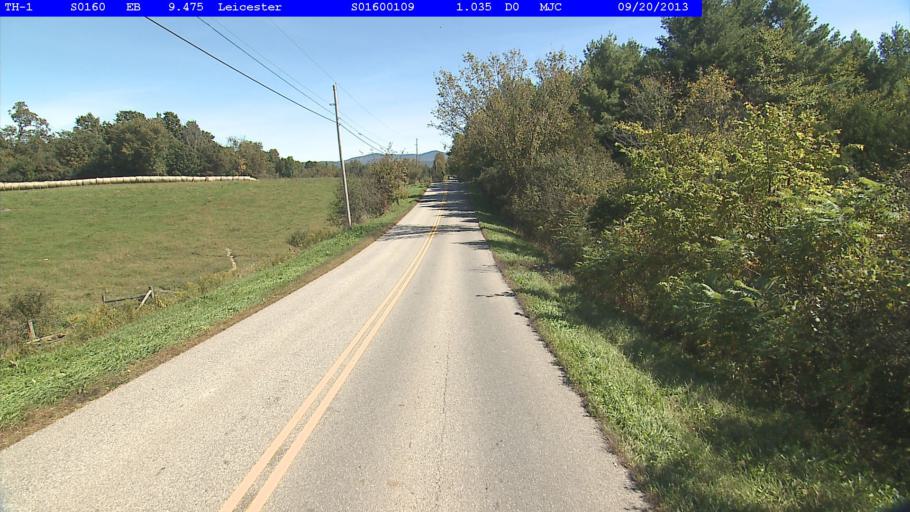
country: US
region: Vermont
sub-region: Rutland County
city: Brandon
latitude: 43.8555
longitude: -73.1393
